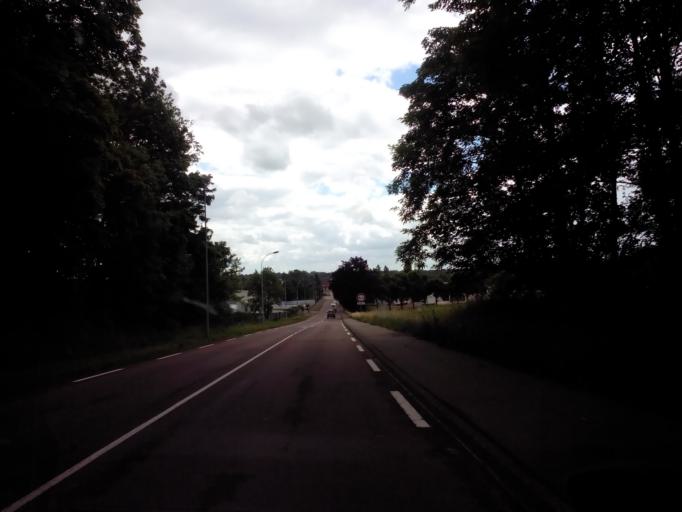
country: FR
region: Bourgogne
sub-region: Departement de la Cote-d'Or
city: Chatillon-sur-Seine
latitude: 47.8749
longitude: 4.5692
